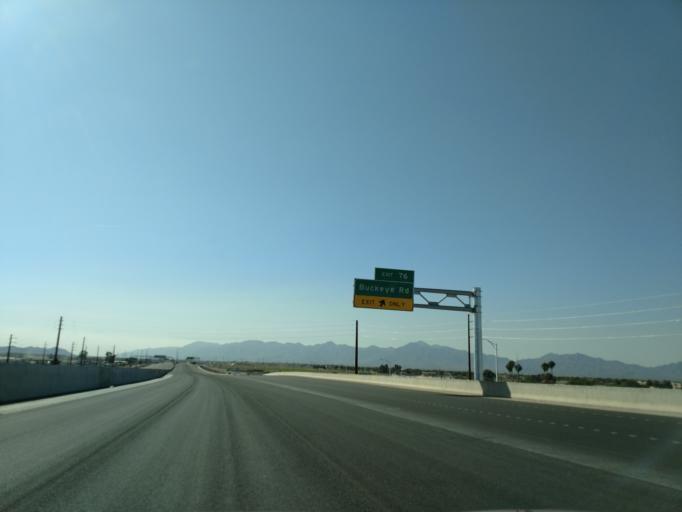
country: US
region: Arizona
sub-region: Maricopa County
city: Tolleson
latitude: 33.4429
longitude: -112.1873
